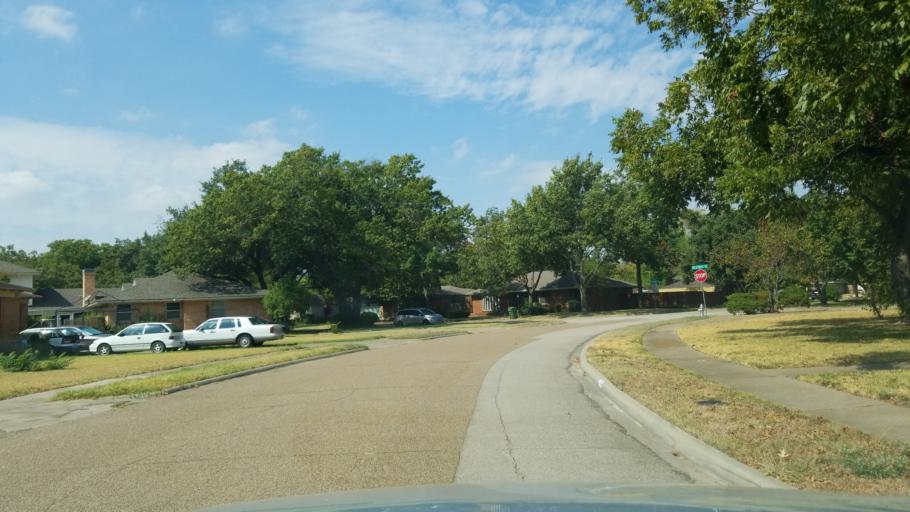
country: US
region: Texas
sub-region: Dallas County
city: Garland
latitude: 32.8982
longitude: -96.6602
